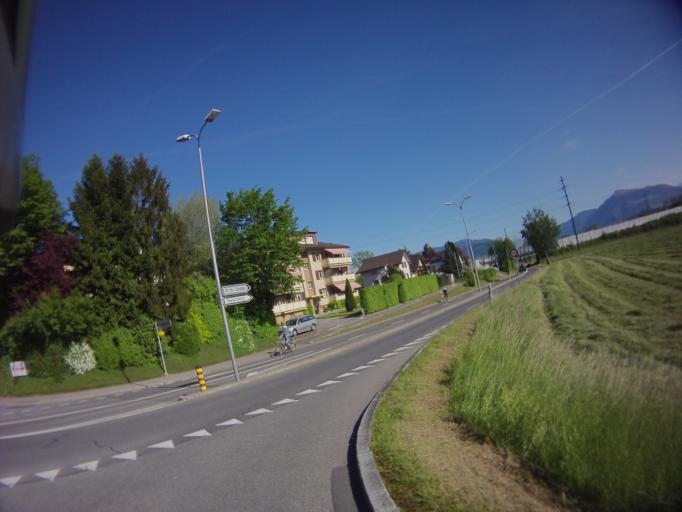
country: CH
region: Zug
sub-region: Zug
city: Cham
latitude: 47.1967
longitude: 8.4525
